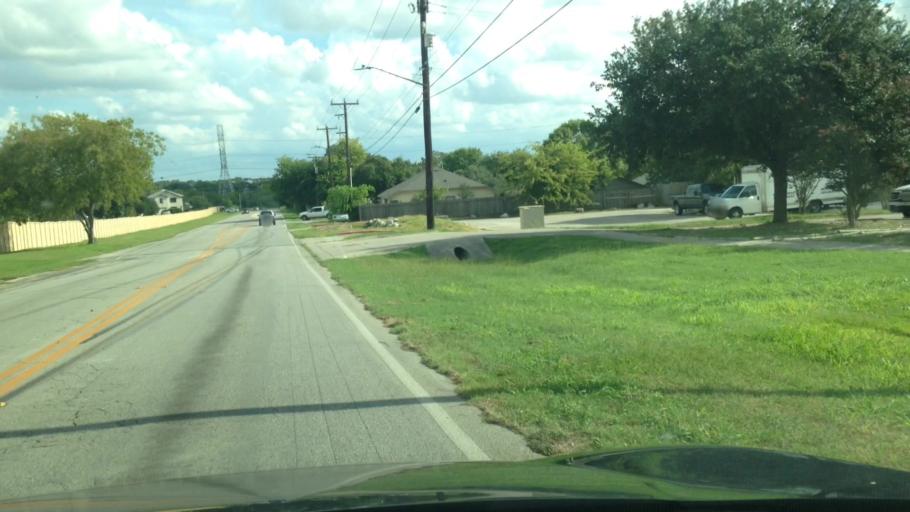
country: US
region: Texas
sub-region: Bexar County
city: Live Oak
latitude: 29.5864
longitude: -98.4063
